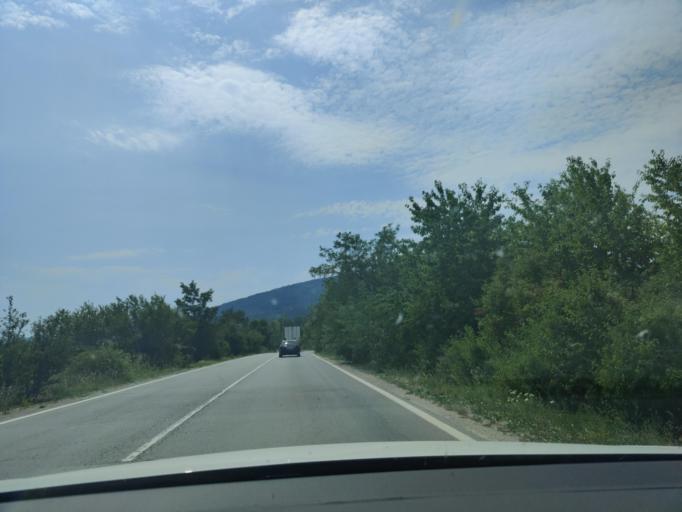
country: BG
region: Montana
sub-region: Obshtina Montana
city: Montana
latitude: 43.4723
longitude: 23.0862
